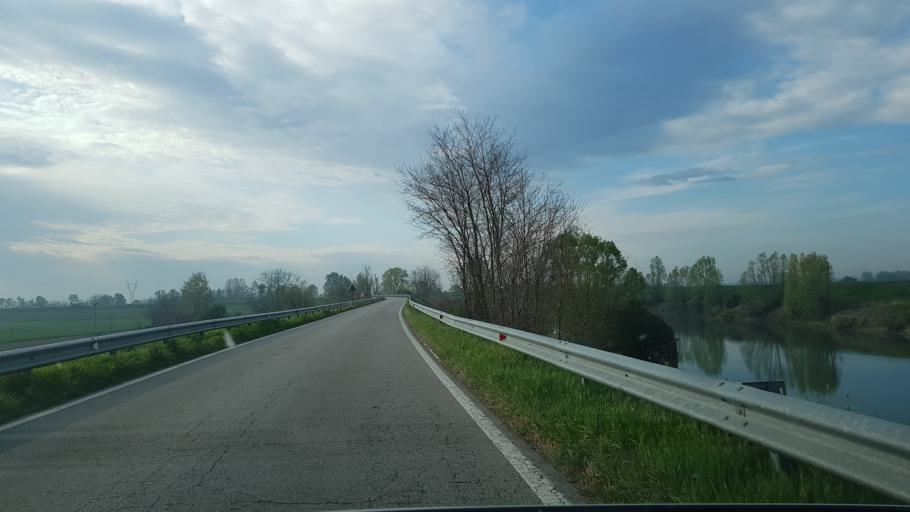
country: IT
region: Veneto
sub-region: Provincia di Padova
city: Piacenza d'Adige
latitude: 45.1225
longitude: 11.5815
